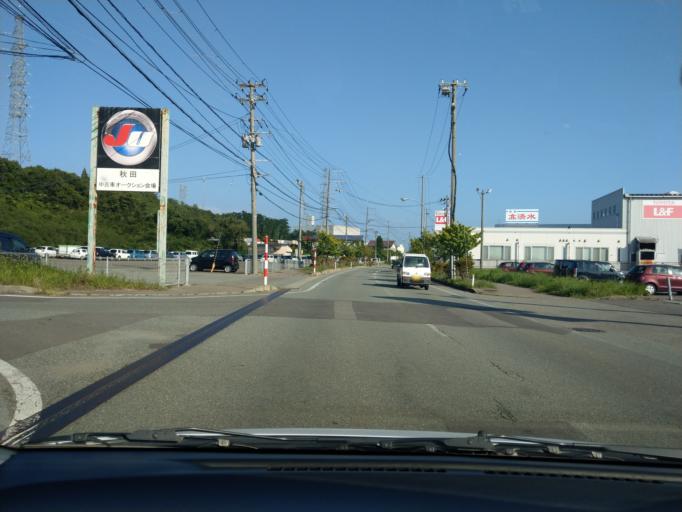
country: JP
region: Akita
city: Akita
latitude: 39.6587
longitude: 140.1728
